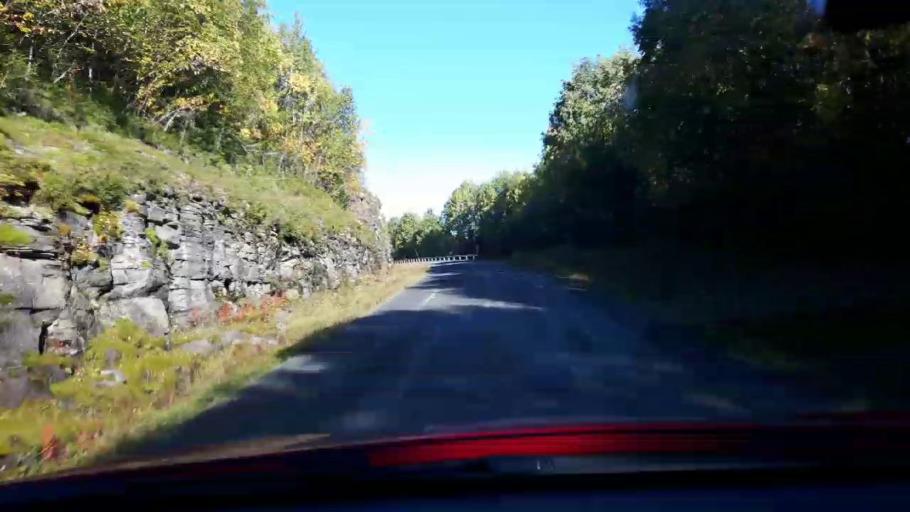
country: NO
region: Nord-Trondelag
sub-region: Lierne
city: Sandvika
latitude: 64.5720
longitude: 13.9024
